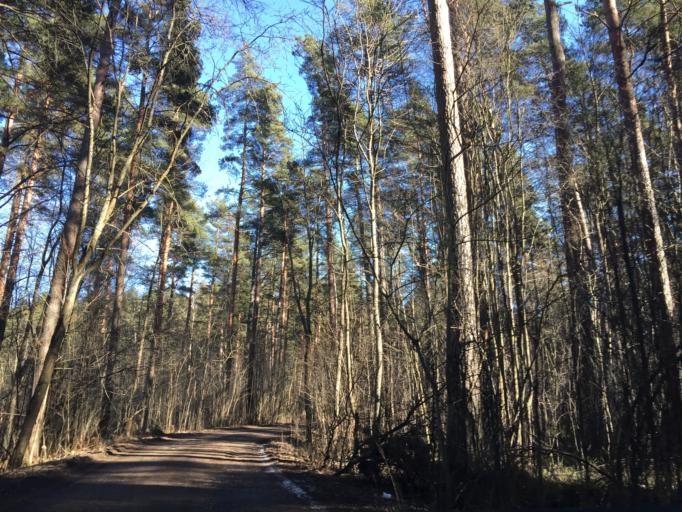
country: LV
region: Babite
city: Pinki
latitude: 56.9673
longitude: 23.9892
